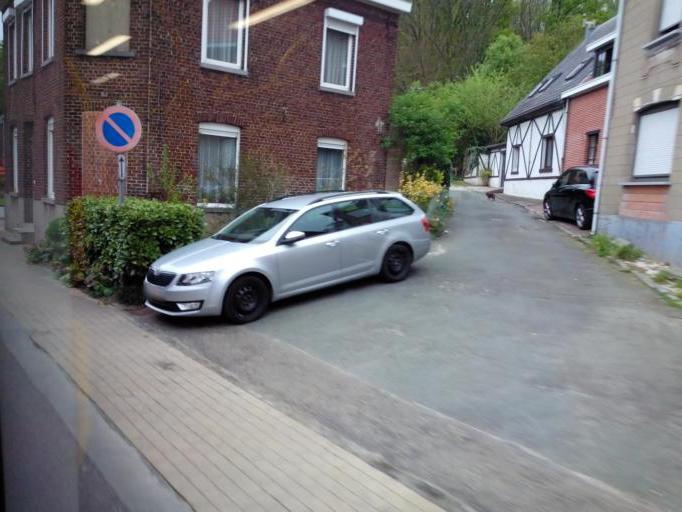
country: BE
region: Flanders
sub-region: Provincie Vlaams-Brabant
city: Kortenberg
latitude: 50.8792
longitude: 4.5409
